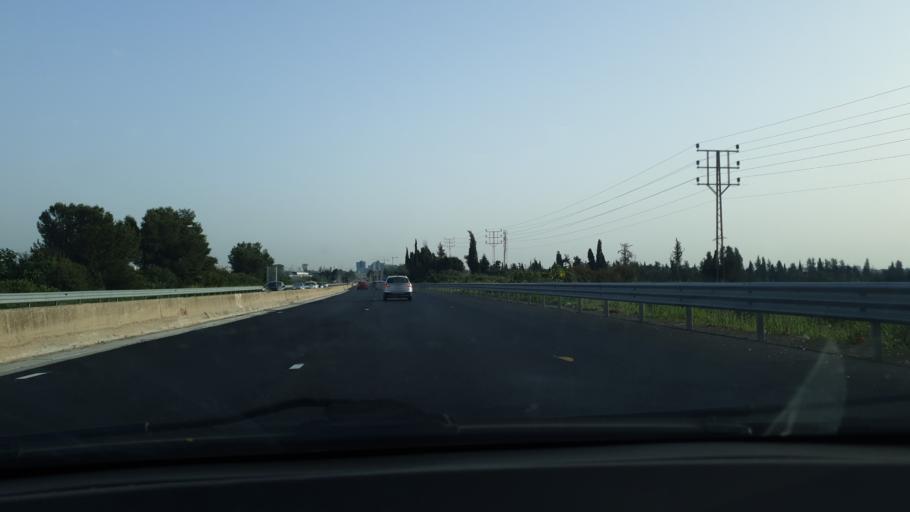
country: IL
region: Central District
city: Tel Mond
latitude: 32.2253
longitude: 34.8828
